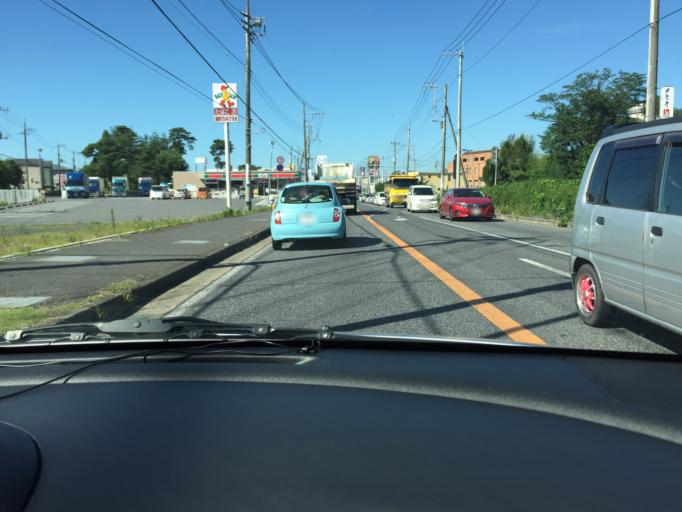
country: JP
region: Ibaraki
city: Naka
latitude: 36.0499
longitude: 140.1705
